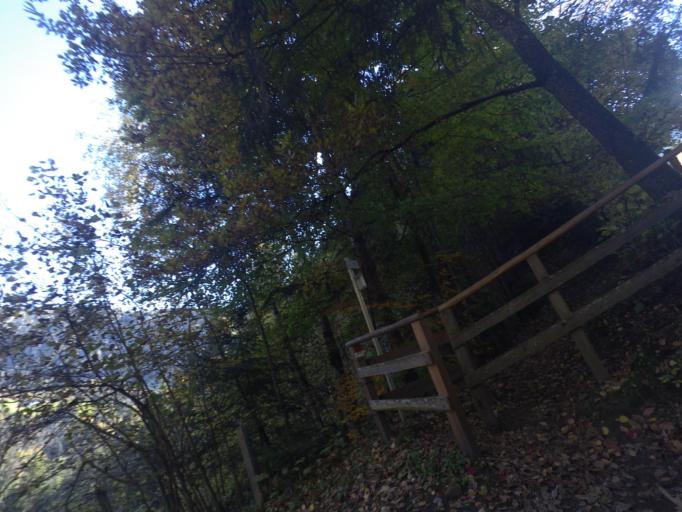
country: AT
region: Salzburg
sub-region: Politischer Bezirk Sankt Johann im Pongau
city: Sankt Johann im Pongau
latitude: 47.3188
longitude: 13.1875
